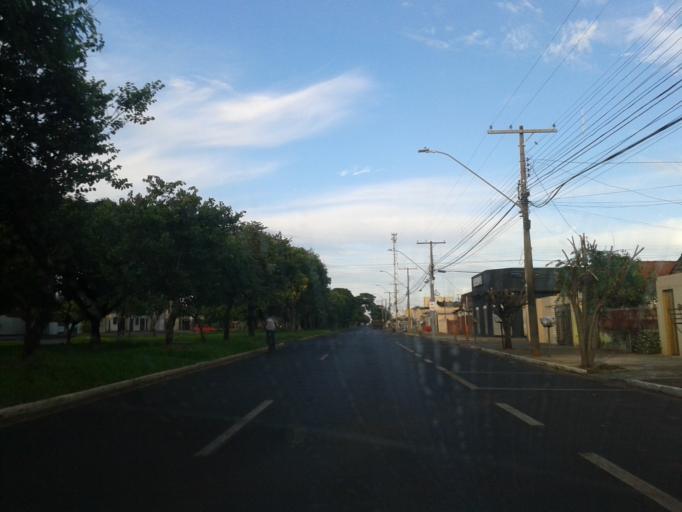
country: BR
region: Minas Gerais
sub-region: Araguari
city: Araguari
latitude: -18.6407
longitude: -48.2062
